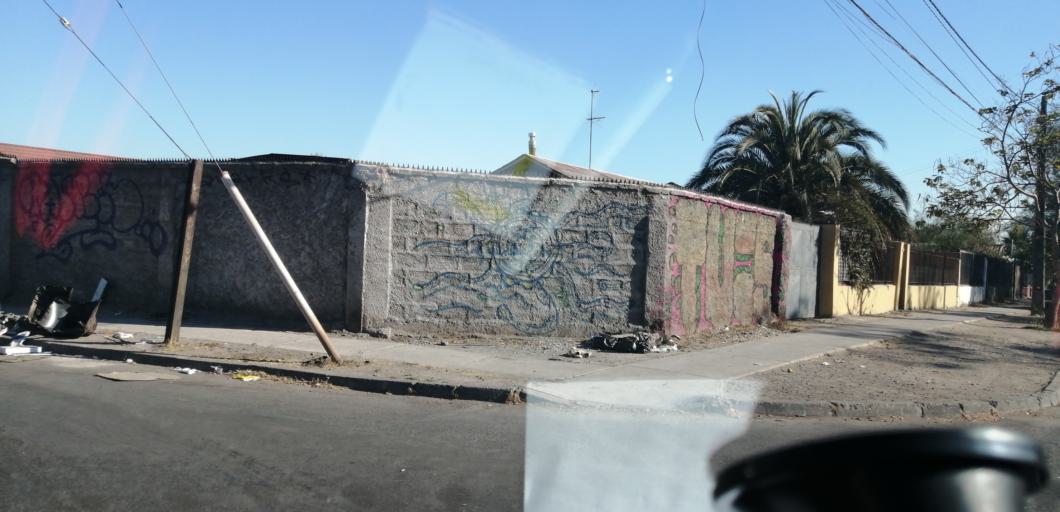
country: CL
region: Santiago Metropolitan
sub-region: Provincia de Santiago
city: Lo Prado
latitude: -33.4372
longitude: -70.7614
